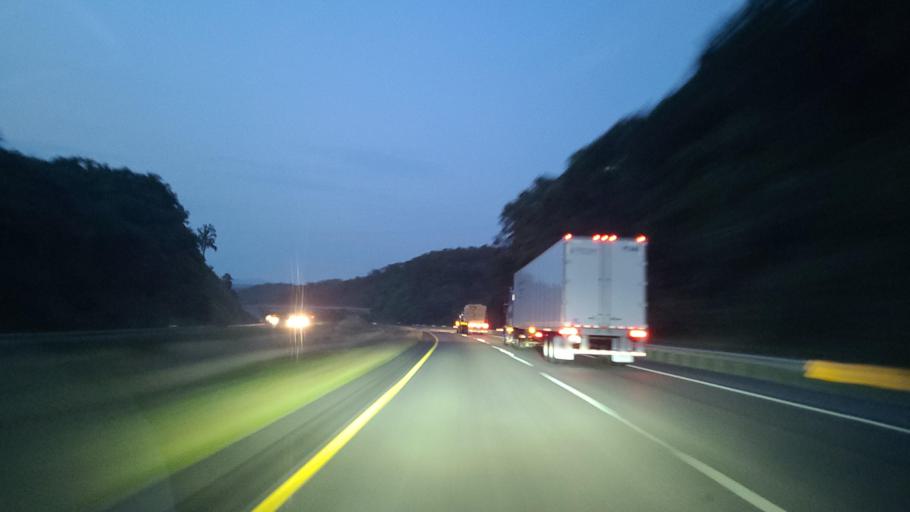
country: US
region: Virginia
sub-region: Montgomery County
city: Shawsville
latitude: 37.1716
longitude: -80.3034
